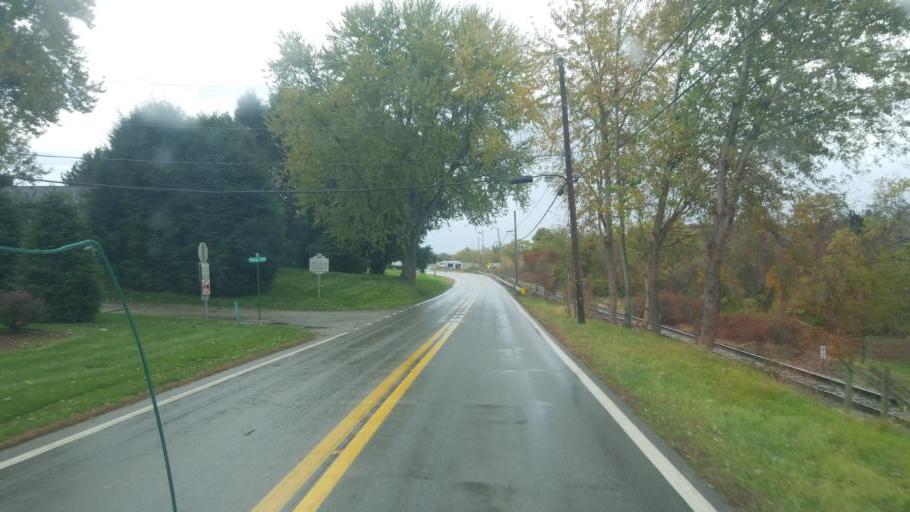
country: US
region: West Virginia
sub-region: Wood County
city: Williamstown
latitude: 39.4011
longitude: -81.4633
